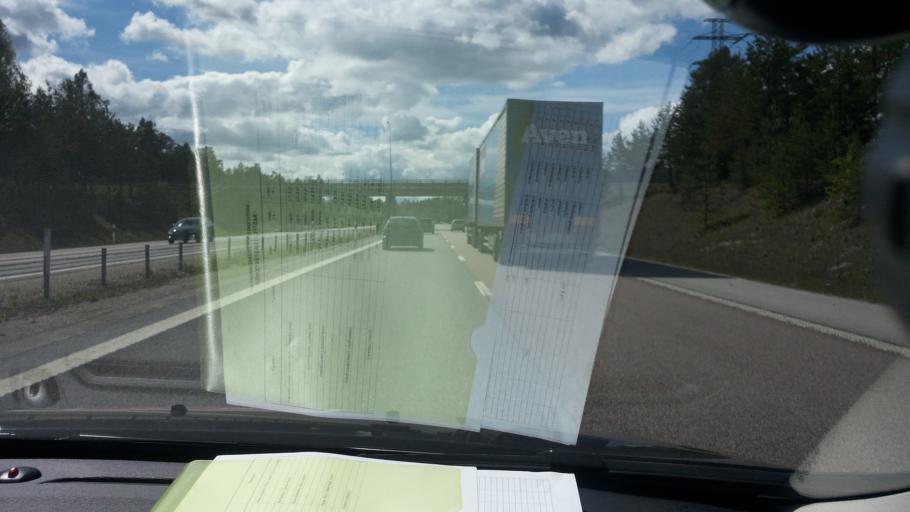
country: SE
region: Vaesternorrland
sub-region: Timra Kommun
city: Timra
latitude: 62.4979
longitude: 17.3388
